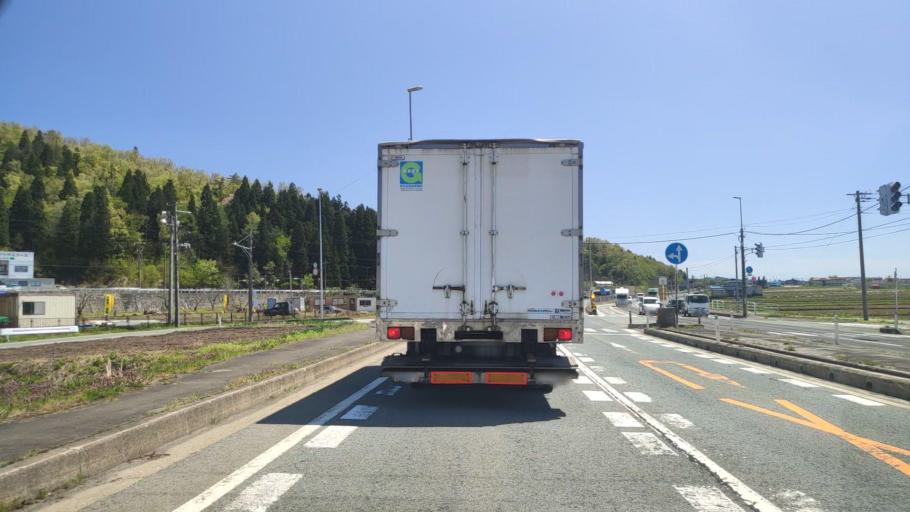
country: JP
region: Yamagata
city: Obanazawa
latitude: 38.5264
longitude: 140.3954
